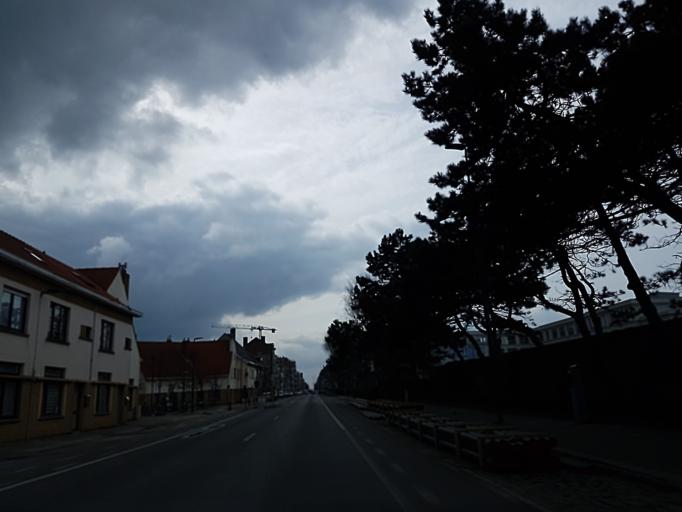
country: BE
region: Flanders
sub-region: Provincie West-Vlaanderen
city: Ostend
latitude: 51.2186
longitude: 2.8956
